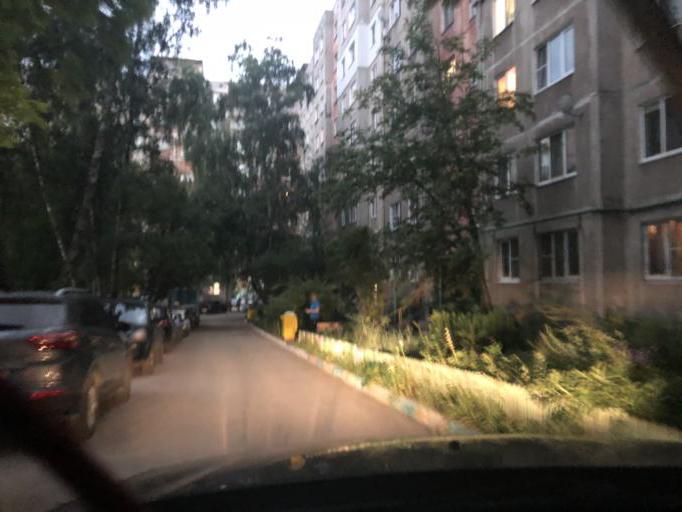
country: RU
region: Tula
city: Tula
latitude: 54.2163
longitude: 37.6091
